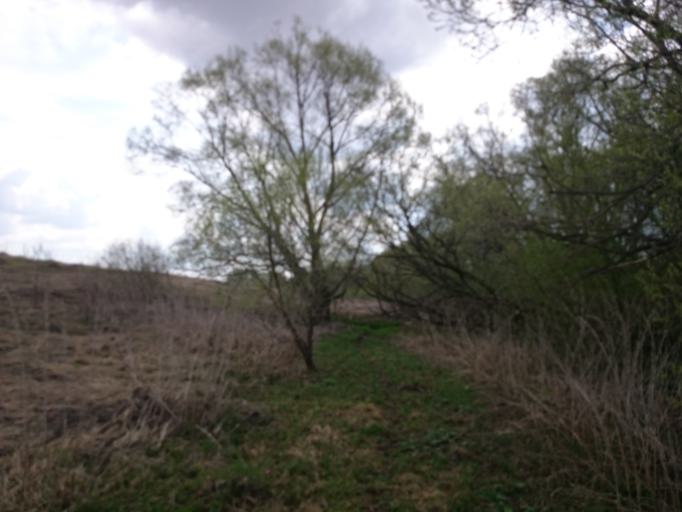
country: RU
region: Mordoviya
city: Kadoshkino
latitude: 54.0319
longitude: 44.4944
